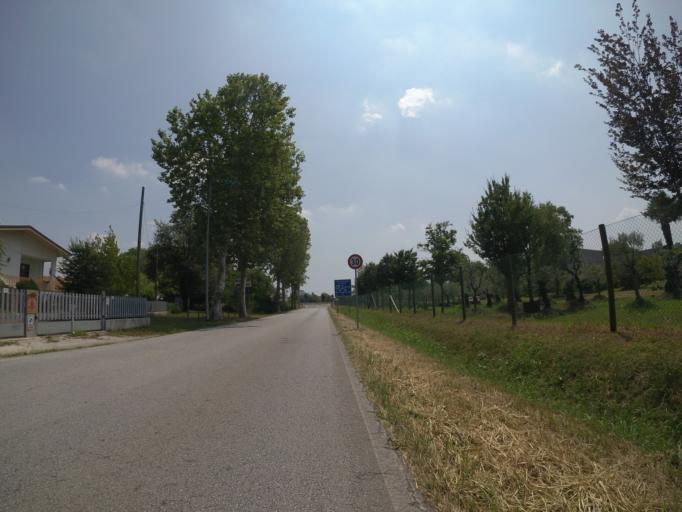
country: IT
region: Friuli Venezia Giulia
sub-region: Provincia di Udine
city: Basiliano-Vissandone
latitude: 46.0078
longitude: 13.1140
